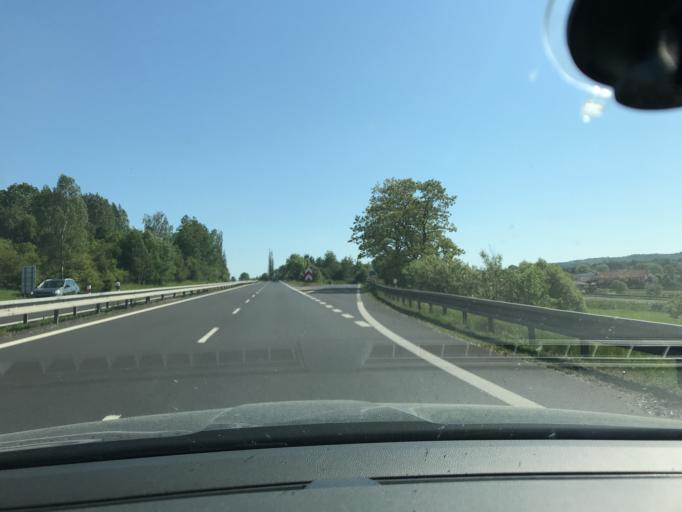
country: CZ
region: Karlovarsky
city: Sadov
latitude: 50.2637
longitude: 12.9234
